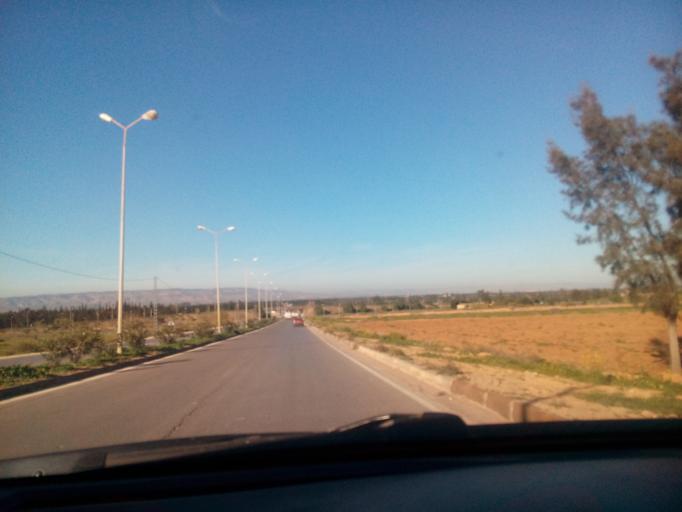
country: DZ
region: Relizane
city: Relizane
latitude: 35.7125
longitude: 0.5082
